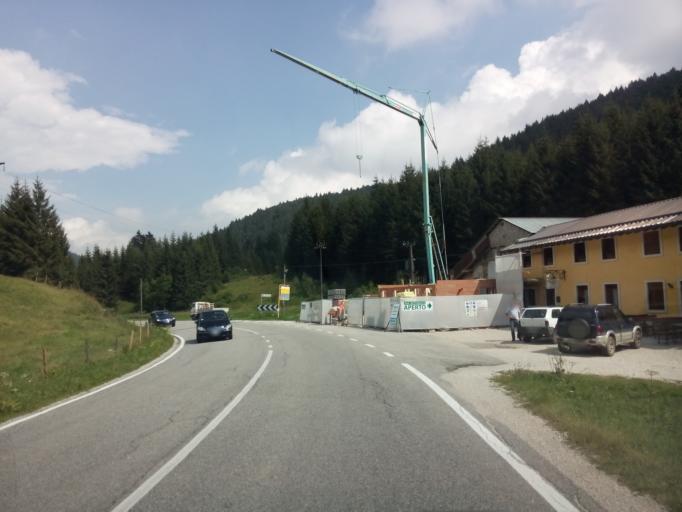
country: IT
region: Veneto
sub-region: Provincia di Vicenza
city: Lusiana
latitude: 45.8346
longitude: 11.5568
